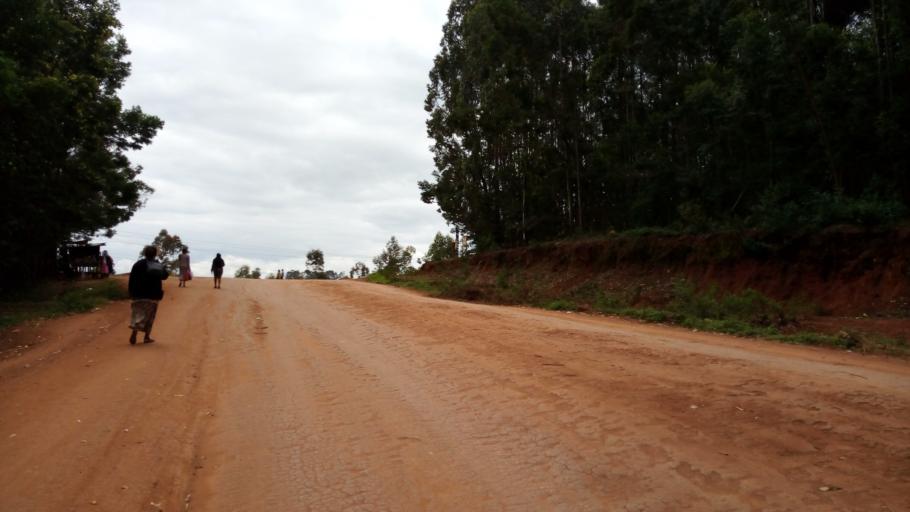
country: KE
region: Makueni
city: Wote
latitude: -1.6580
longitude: 37.4535
